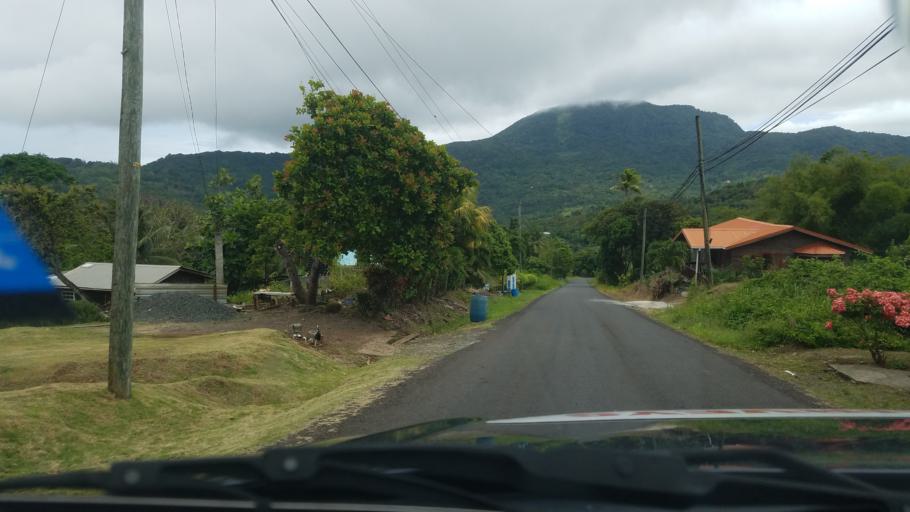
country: LC
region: Castries Quarter
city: Bisee
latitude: 14.0156
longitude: -60.9287
